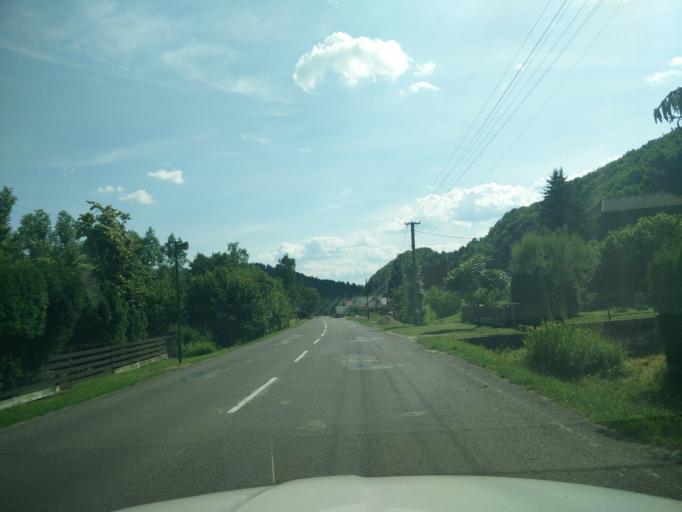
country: SK
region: Nitriansky
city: Prievidza
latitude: 48.9051
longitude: 18.6520
